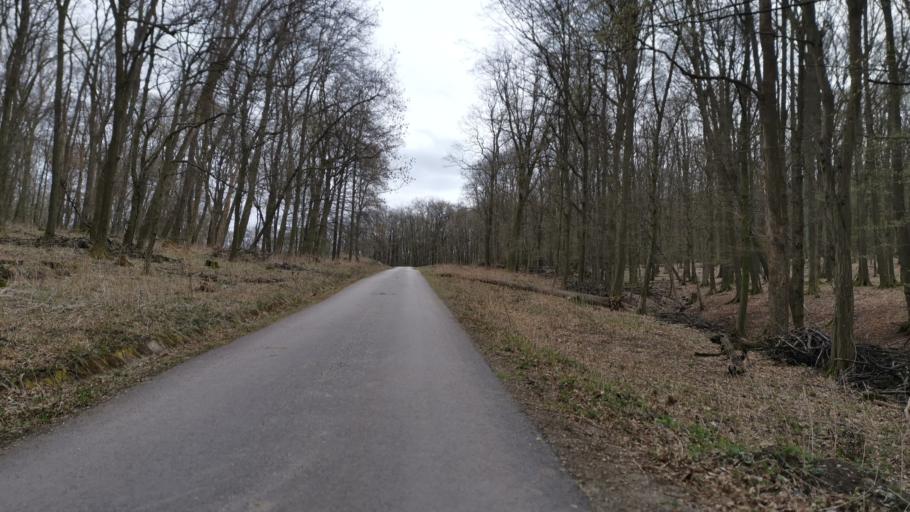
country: CZ
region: South Moravian
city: Petrov
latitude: 48.8082
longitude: 17.3258
